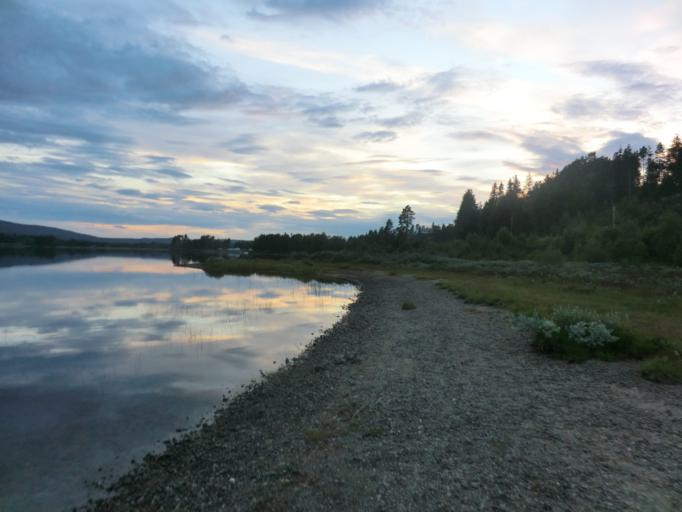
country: NO
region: Hedmark
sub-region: Trysil
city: Innbygda
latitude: 61.8531
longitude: 12.7448
